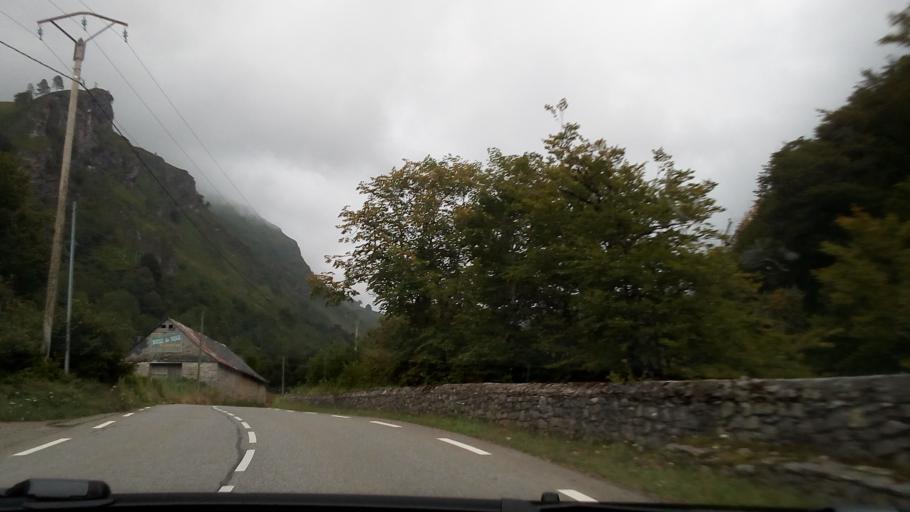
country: FR
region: Aquitaine
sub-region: Departement des Pyrenees-Atlantiques
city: Laruns
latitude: 42.9675
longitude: -0.3743
